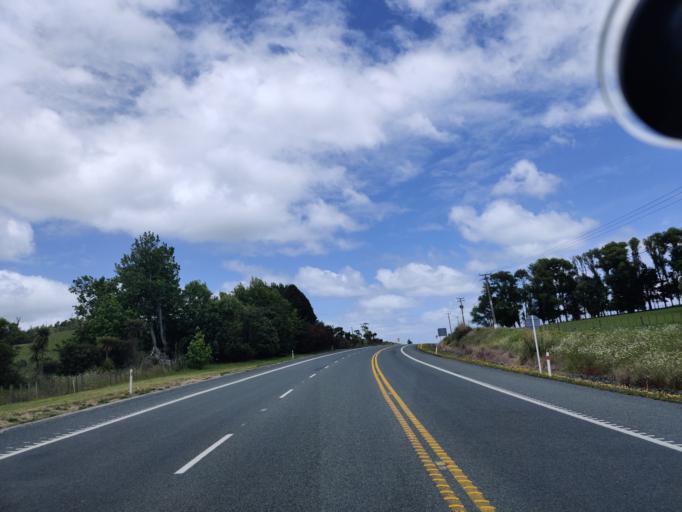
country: NZ
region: Auckland
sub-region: Auckland
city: Wellsford
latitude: -36.2388
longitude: 174.5113
